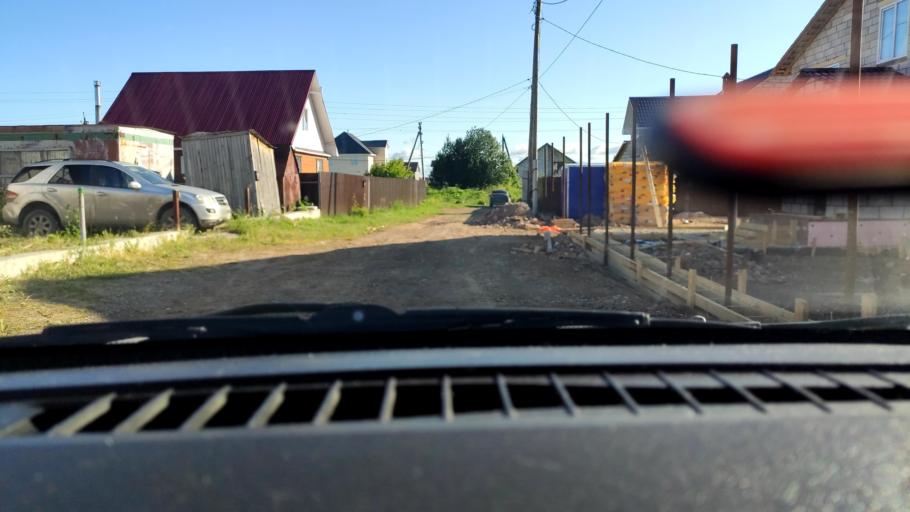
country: RU
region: Perm
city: Kultayevo
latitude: 57.8627
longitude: 55.9113
